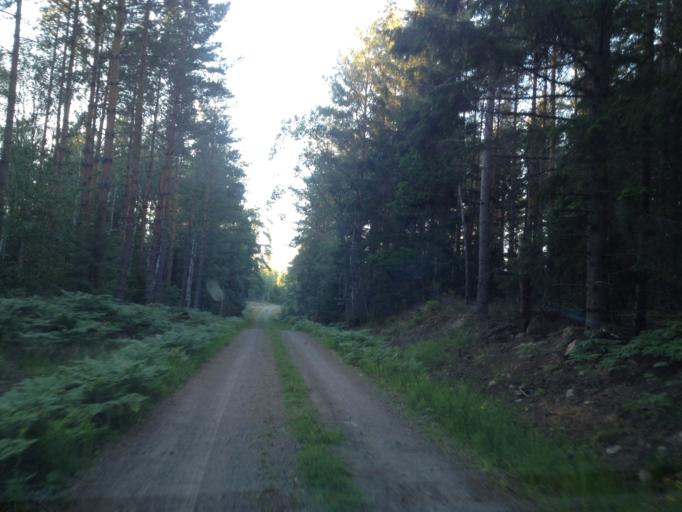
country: SE
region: Kalmar
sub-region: Vasterviks Kommun
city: Overum
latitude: 57.9936
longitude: 16.1698
